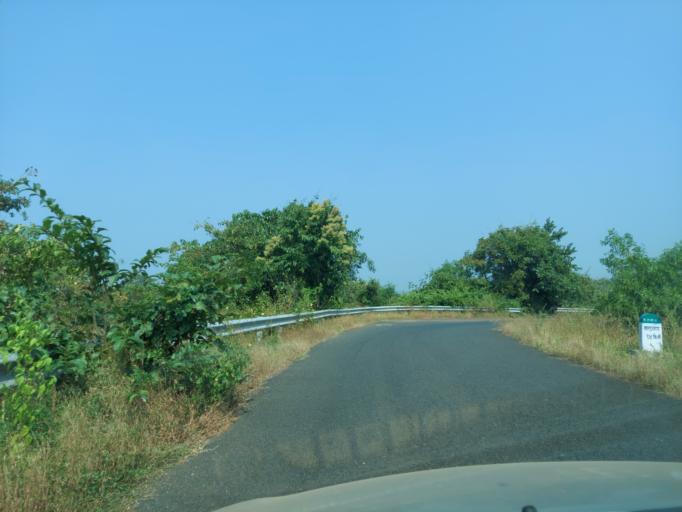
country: IN
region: Maharashtra
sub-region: Sindhudurg
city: Malvan
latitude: 16.0019
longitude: 73.5080
